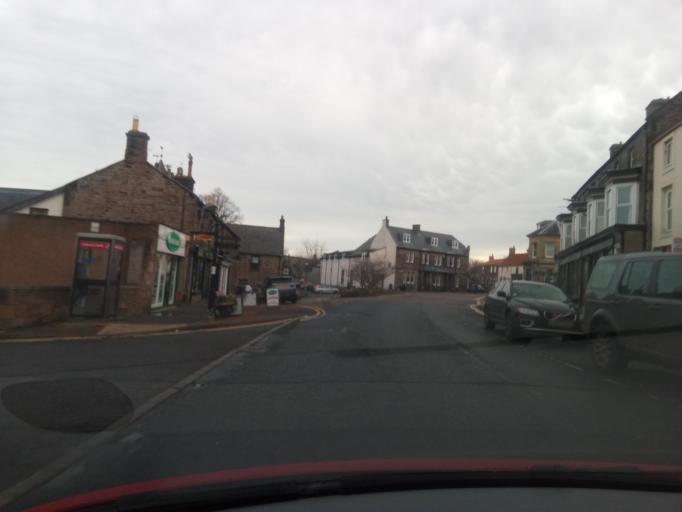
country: GB
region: England
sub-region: Northumberland
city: Wooler
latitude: 55.5461
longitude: -2.0152
